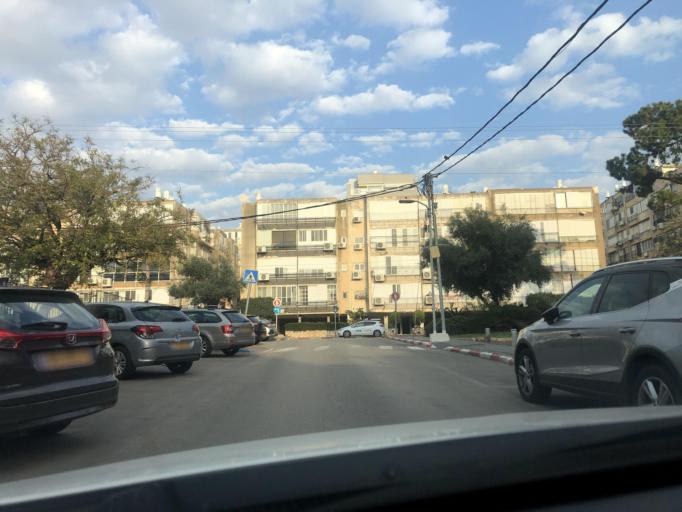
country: IL
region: Tel Aviv
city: Bat Yam
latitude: 32.0197
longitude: 34.7497
